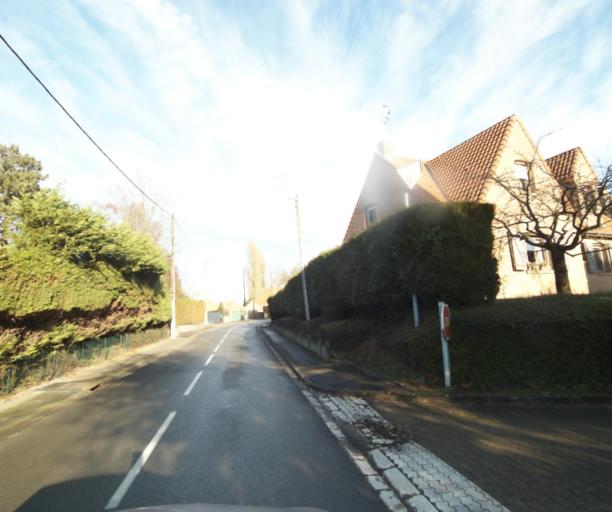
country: FR
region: Nord-Pas-de-Calais
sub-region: Departement du Nord
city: Curgies
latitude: 50.3526
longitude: 3.5982
